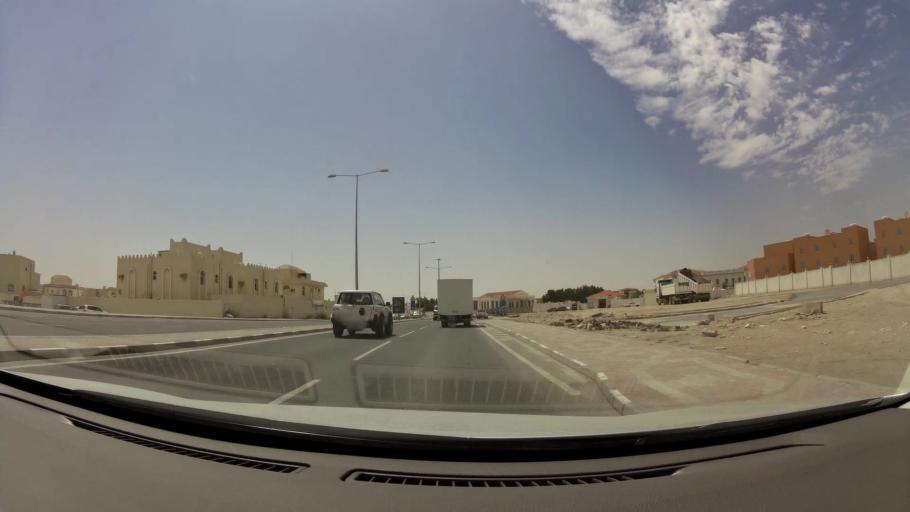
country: QA
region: Baladiyat ar Rayyan
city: Ar Rayyan
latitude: 25.2617
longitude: 51.4199
